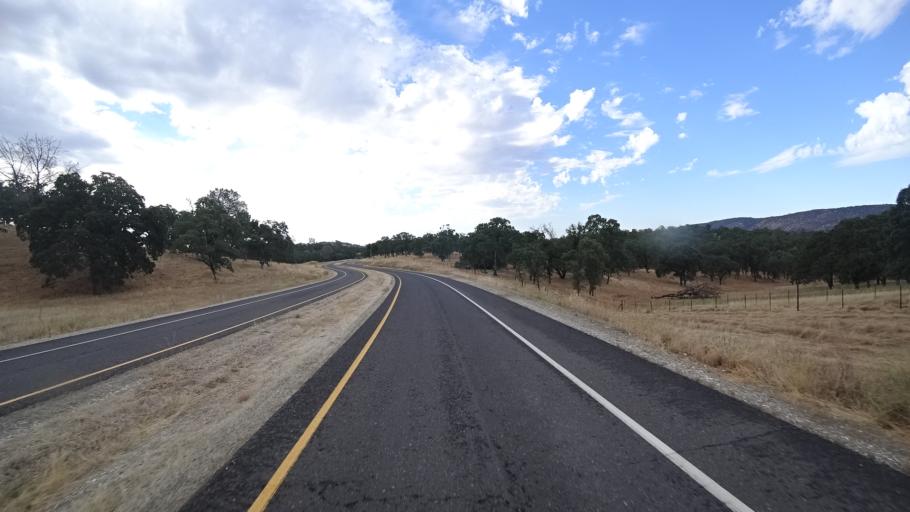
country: US
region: California
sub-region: Calaveras County
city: Copperopolis
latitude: 37.9448
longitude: -120.6501
